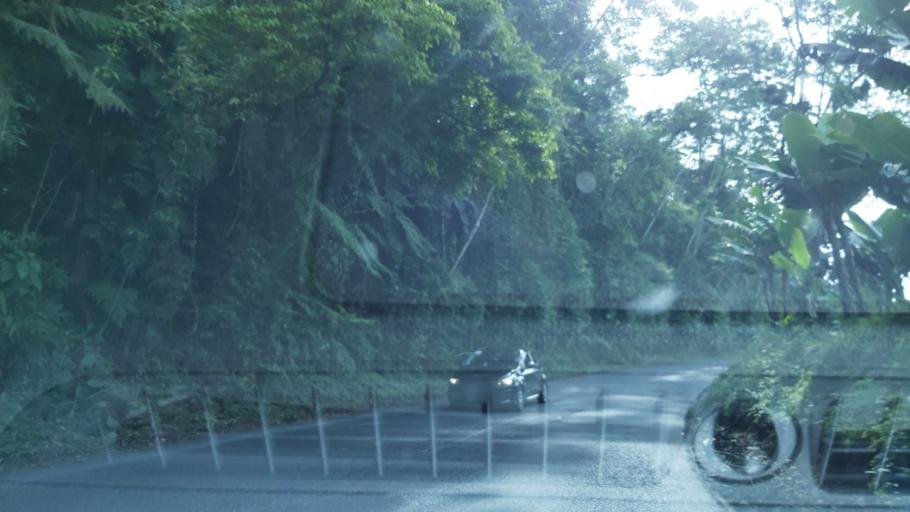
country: BR
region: Sao Paulo
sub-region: Juquia
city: Juquia
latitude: -24.0847
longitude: -47.6113
